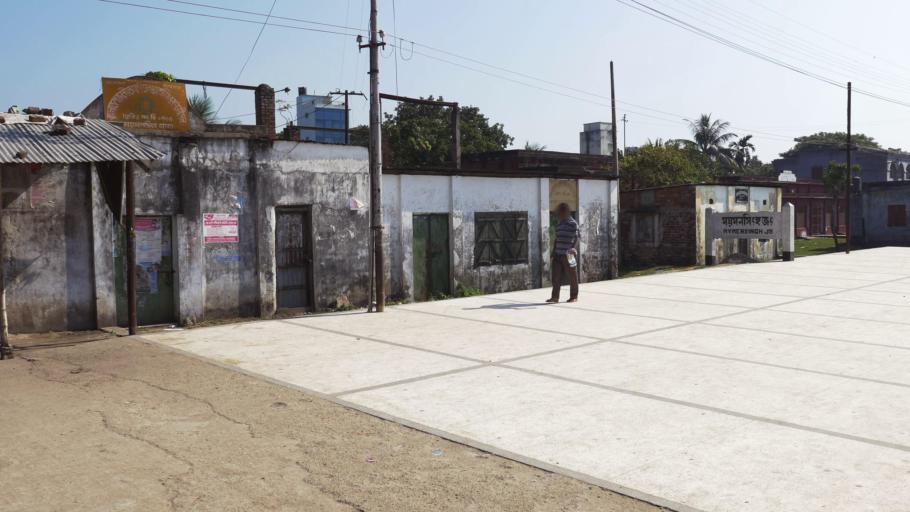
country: BD
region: Dhaka
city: Mymensingh
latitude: 24.6555
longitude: 90.4541
